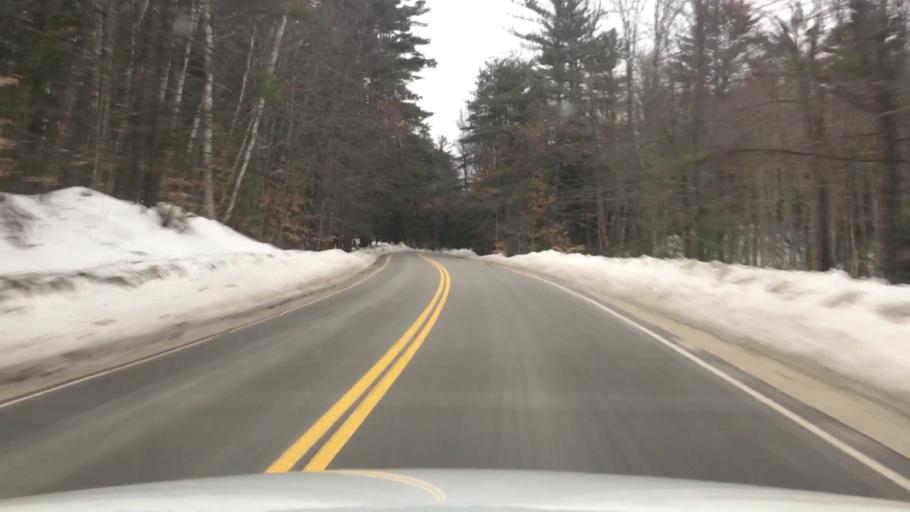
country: US
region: Maine
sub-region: Oxford County
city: Hiram
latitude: 43.8918
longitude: -70.7902
